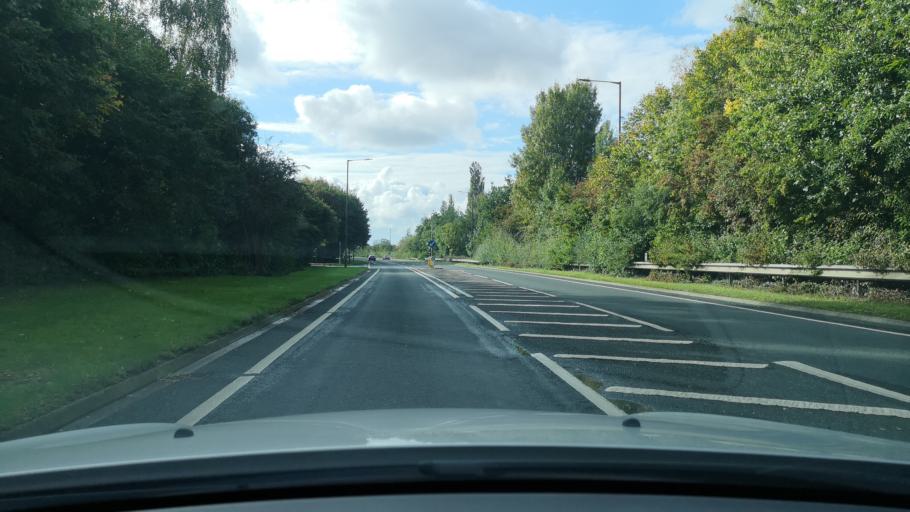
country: GB
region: England
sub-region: East Riding of Yorkshire
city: Beverley
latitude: 53.8585
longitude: -0.4370
